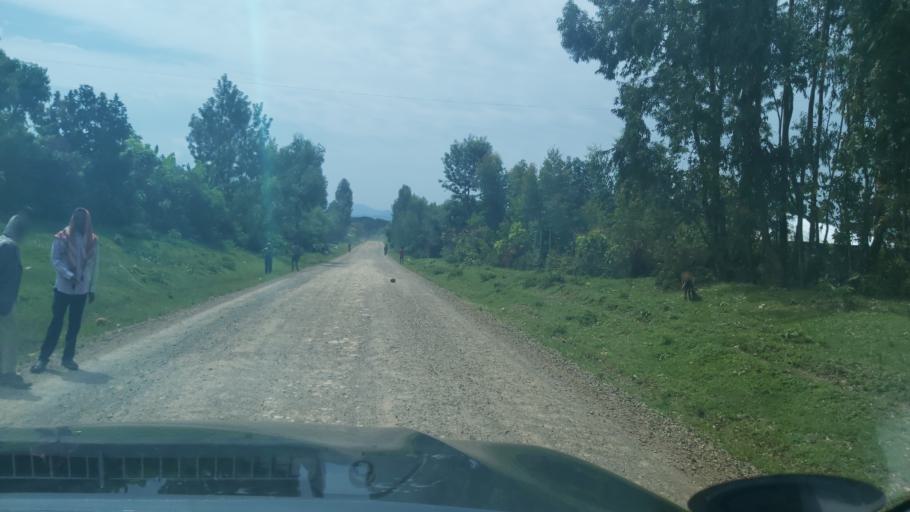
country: ET
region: Oromiya
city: Jima
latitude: 7.7403
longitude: 36.7772
